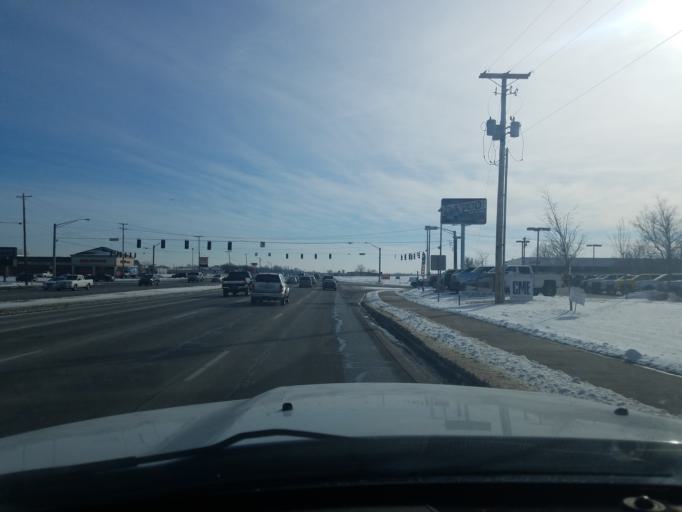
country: US
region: Indiana
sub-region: Allen County
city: Fort Wayne
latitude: 41.1476
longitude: -85.1648
